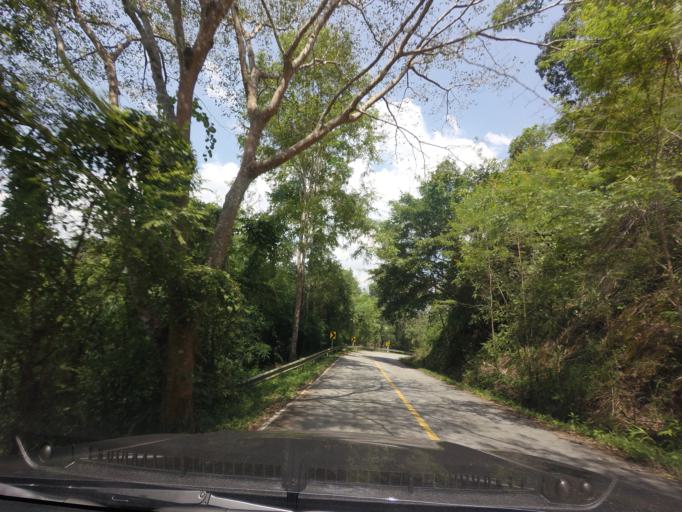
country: TH
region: Loei
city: Na Haeo
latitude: 17.6314
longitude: 100.9027
